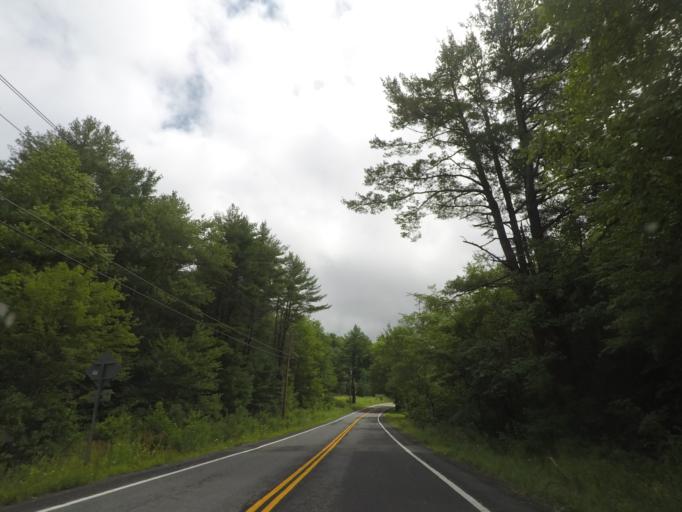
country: US
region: New York
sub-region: Rensselaer County
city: Averill Park
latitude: 42.5950
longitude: -73.5060
